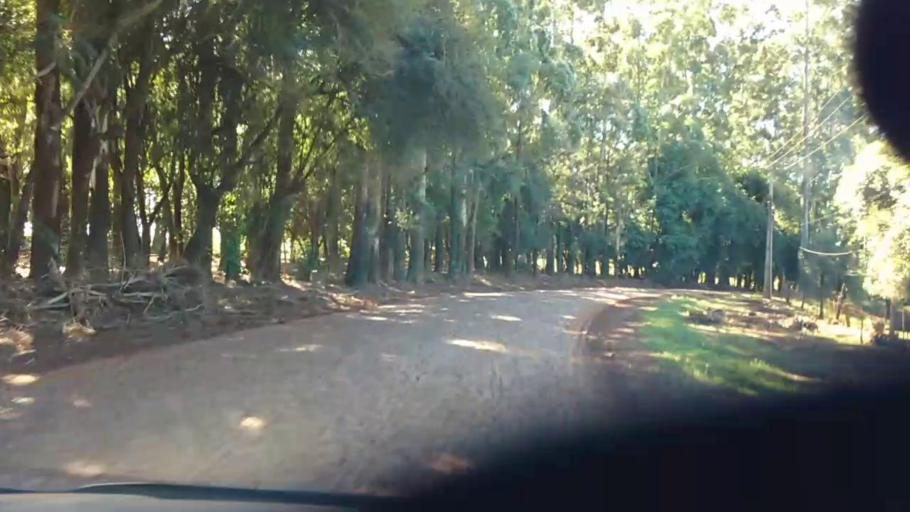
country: PY
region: Alto Parana
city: Naranjal
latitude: -25.9594
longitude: -55.1421
